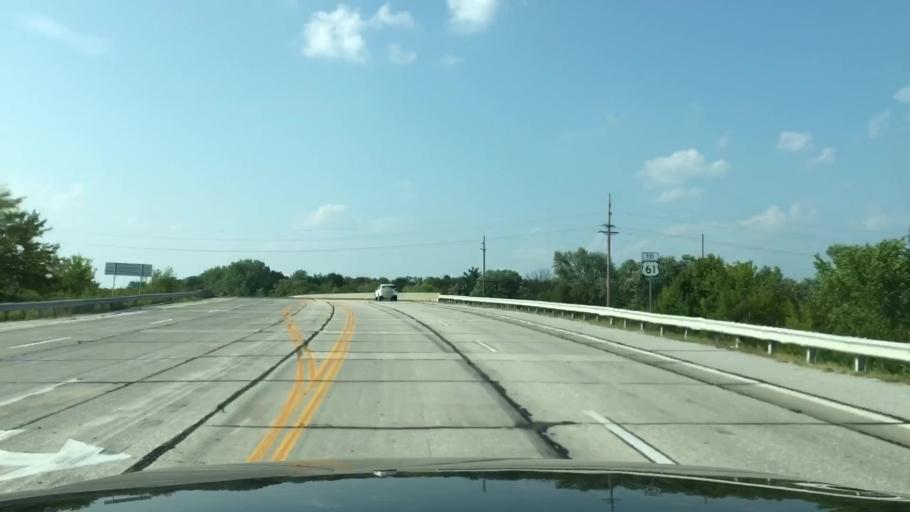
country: US
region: Missouri
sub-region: Saint Charles County
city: Lake Saint Louis
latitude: 38.8081
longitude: -90.8075
